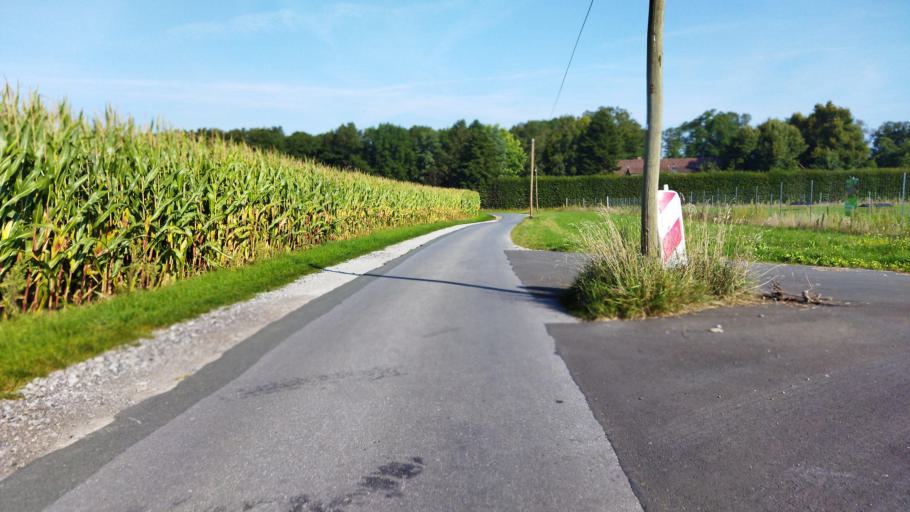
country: DE
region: Lower Saxony
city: Bad Laer
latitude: 52.1167
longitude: 8.0745
